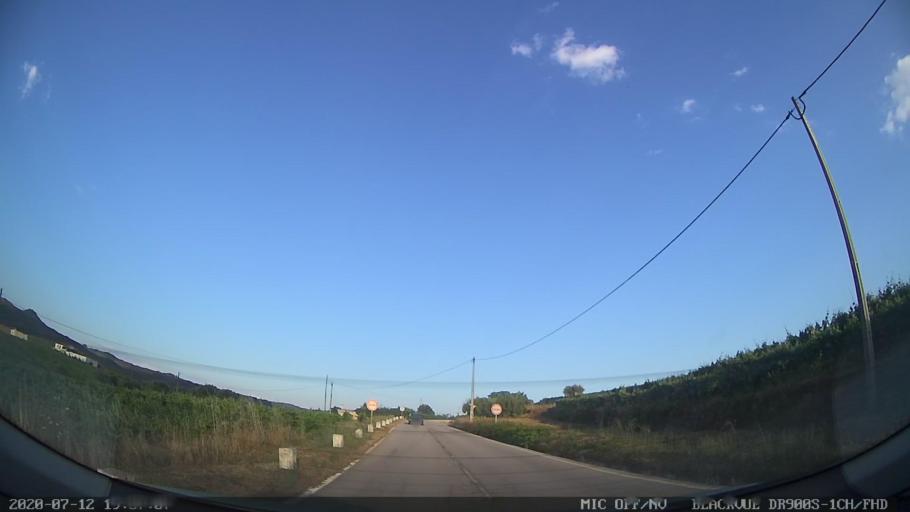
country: PT
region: Vila Real
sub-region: Sabrosa
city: Sabrosa
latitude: 41.2703
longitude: -7.4570
